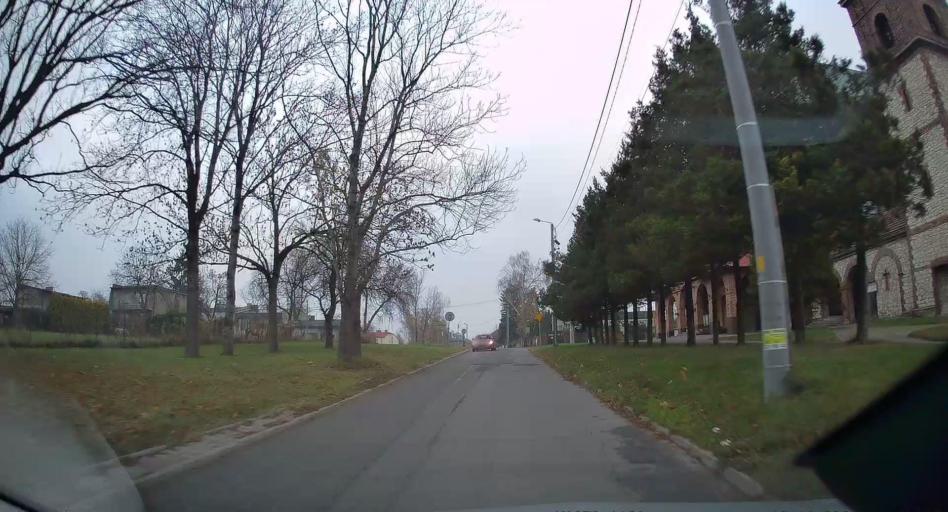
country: PL
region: Silesian Voivodeship
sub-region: Czestochowa
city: Czestochowa
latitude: 50.8178
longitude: 19.0941
